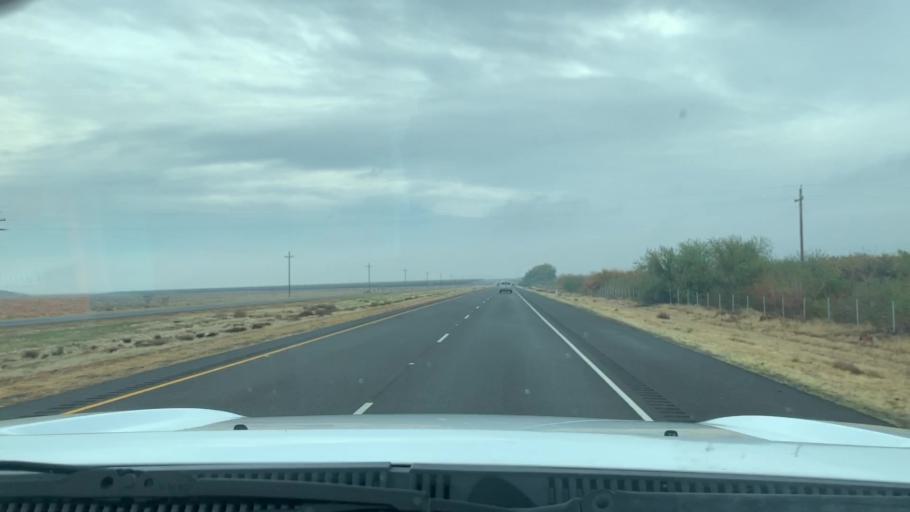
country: US
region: California
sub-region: San Luis Obispo County
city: Shandon
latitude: 35.6814
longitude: -120.1039
